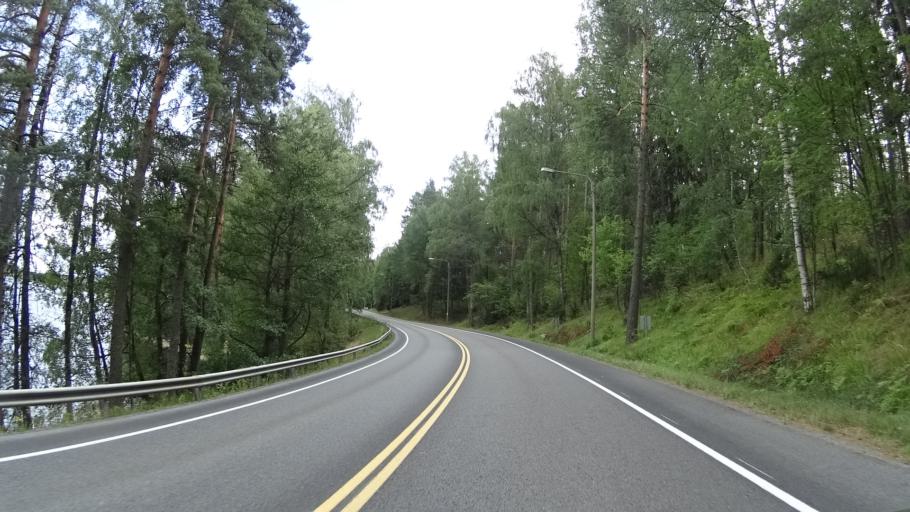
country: FI
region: Pirkanmaa
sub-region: Tampere
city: Kangasala
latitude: 61.4155
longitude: 24.1467
